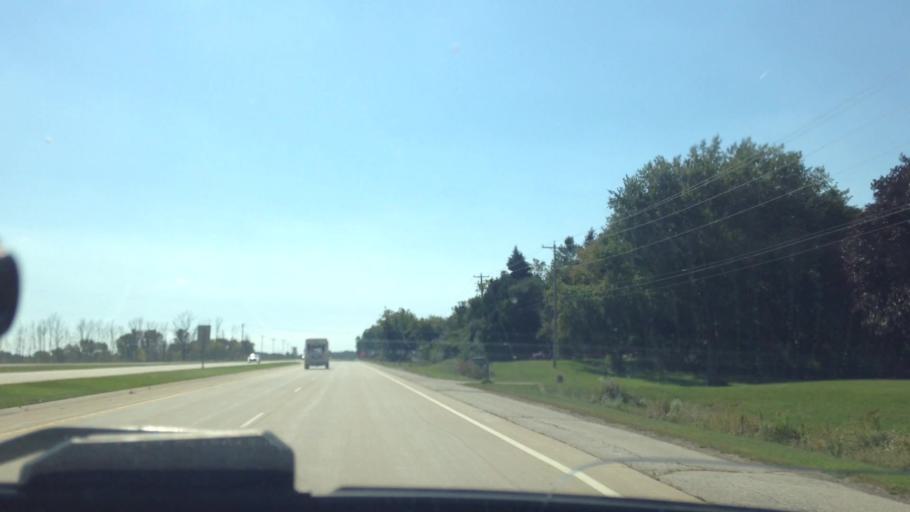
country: US
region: Wisconsin
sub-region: Ozaukee County
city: Saukville
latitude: 43.3487
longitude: -87.9174
